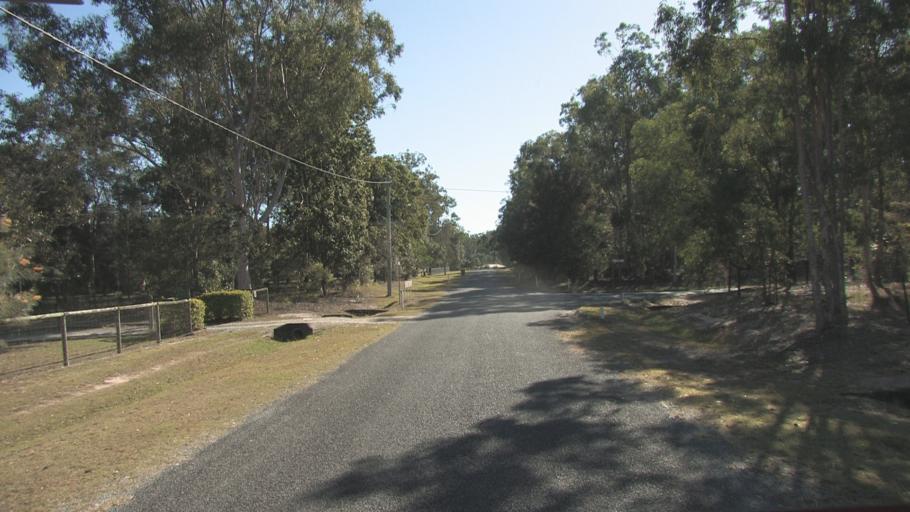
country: AU
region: Queensland
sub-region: Logan
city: Chambers Flat
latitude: -27.7867
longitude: 153.1259
